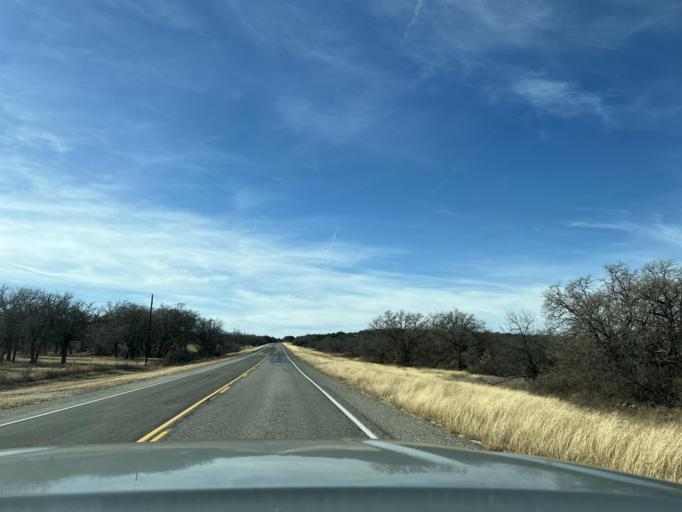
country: US
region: Texas
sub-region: Eastland County
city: Cisco
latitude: 32.4646
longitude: -99.0225
